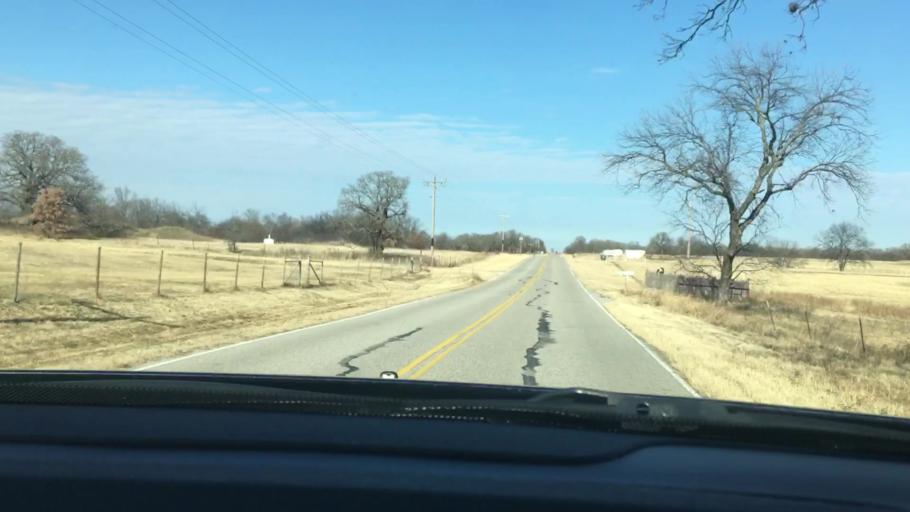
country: US
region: Oklahoma
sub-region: Garvin County
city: Wynnewood
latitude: 34.7269
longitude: -97.1255
